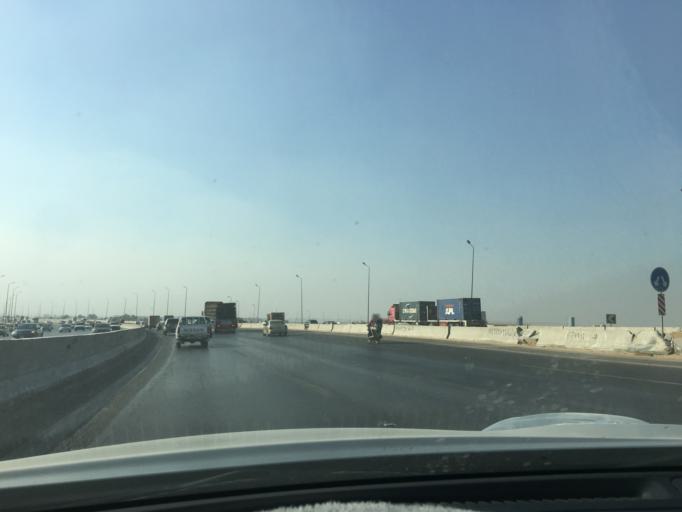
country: EG
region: Muhafazat al Qalyubiyah
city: Al Khankah
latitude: 30.1293
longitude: 31.4646
